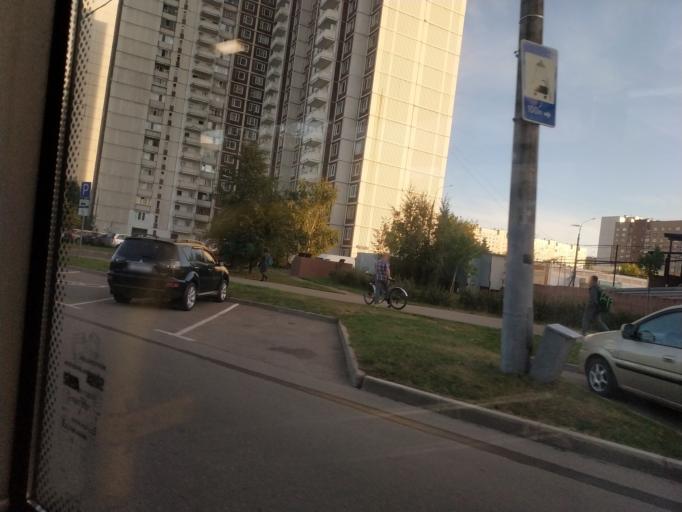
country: RU
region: Moscow
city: Novo-Peredelkino
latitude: 55.6462
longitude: 37.3479
